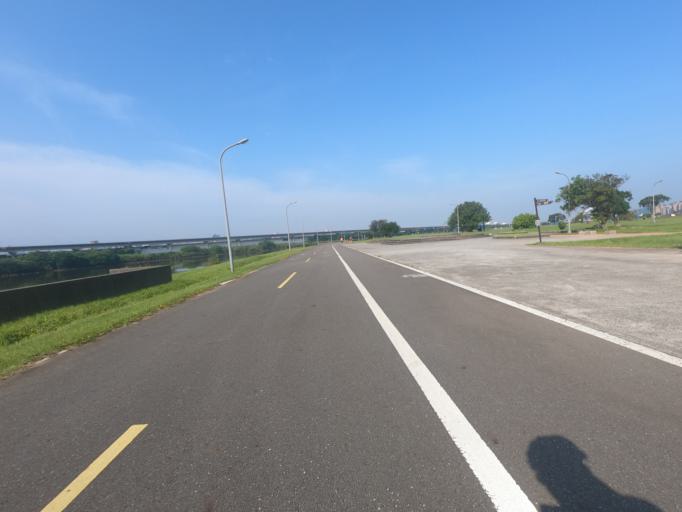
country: TW
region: Taipei
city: Taipei
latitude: 25.0742
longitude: 121.5641
